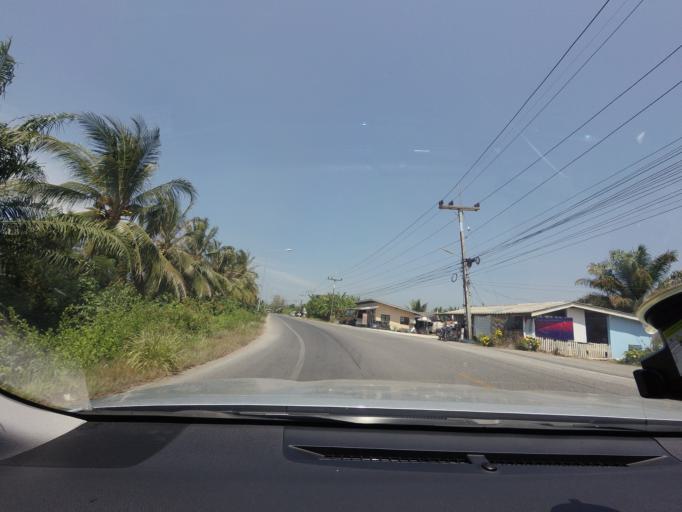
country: TH
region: Surat Thani
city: Tha Chang
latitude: 9.2011
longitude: 99.2457
